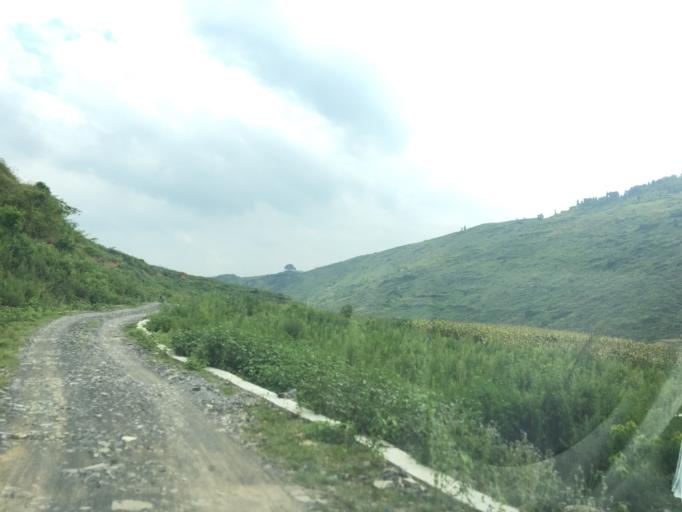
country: CN
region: Guangxi Zhuangzu Zizhiqu
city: Xinzhou
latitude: 25.1952
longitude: 105.7338
